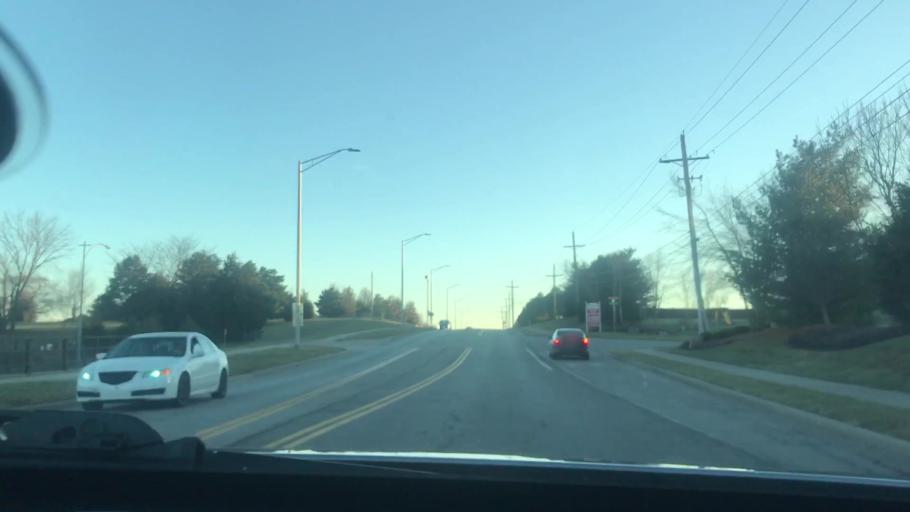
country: US
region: Kansas
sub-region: Johnson County
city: Olathe
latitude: 38.9326
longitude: -94.8161
